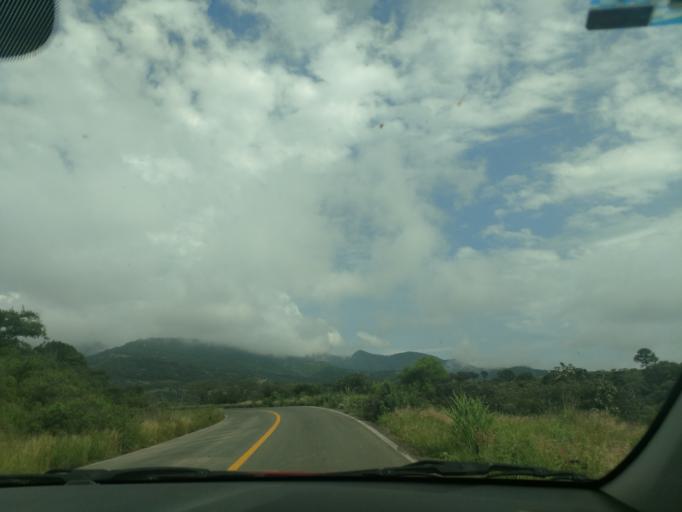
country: MX
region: Jalisco
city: El Salto
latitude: 20.3828
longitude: -104.5452
